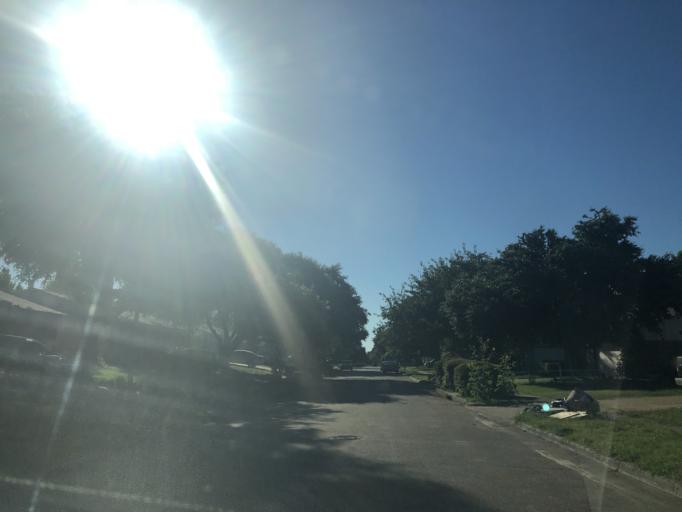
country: US
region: Texas
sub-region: Dallas County
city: Duncanville
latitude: 32.6439
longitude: -96.9506
